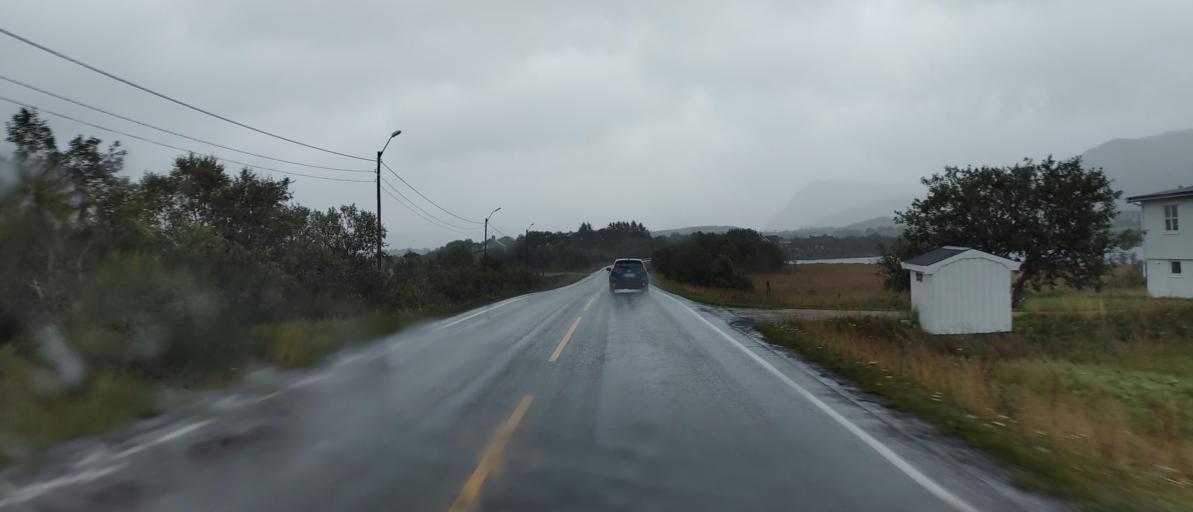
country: NO
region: Nordland
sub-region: Vestvagoy
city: Evjen
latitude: 68.2111
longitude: 13.7047
